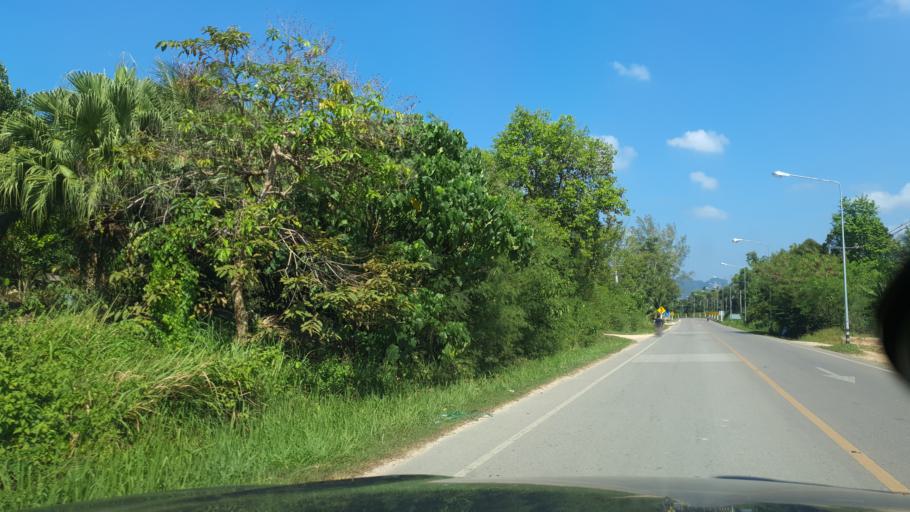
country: TH
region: Phangnga
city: Ban Ao Nang
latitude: 8.0411
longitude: 98.8614
